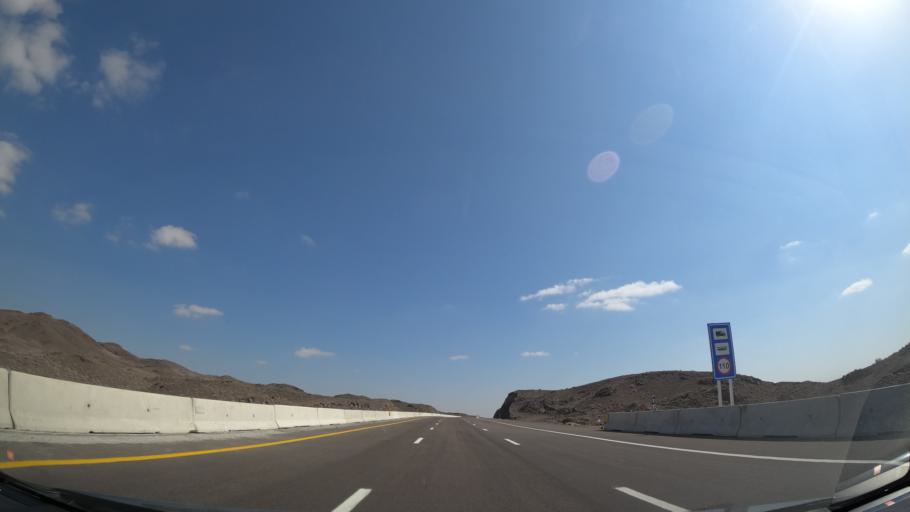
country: IR
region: Alborz
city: Nazarabad
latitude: 35.6610
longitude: 50.6567
